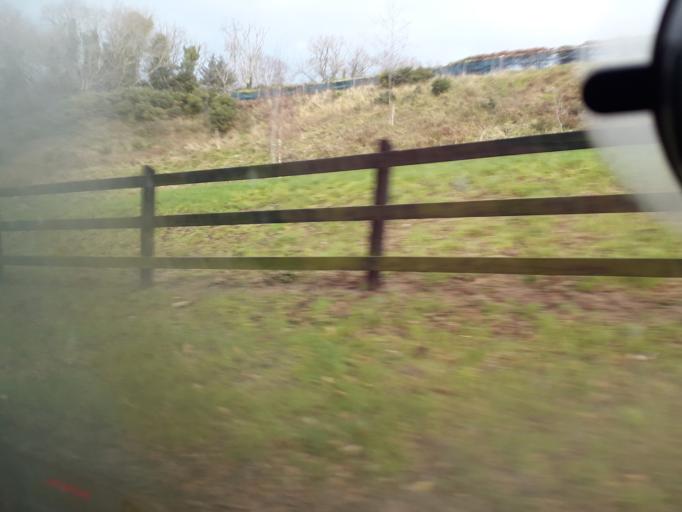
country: IE
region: Leinster
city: Ballyboden
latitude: 53.2508
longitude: -6.3008
